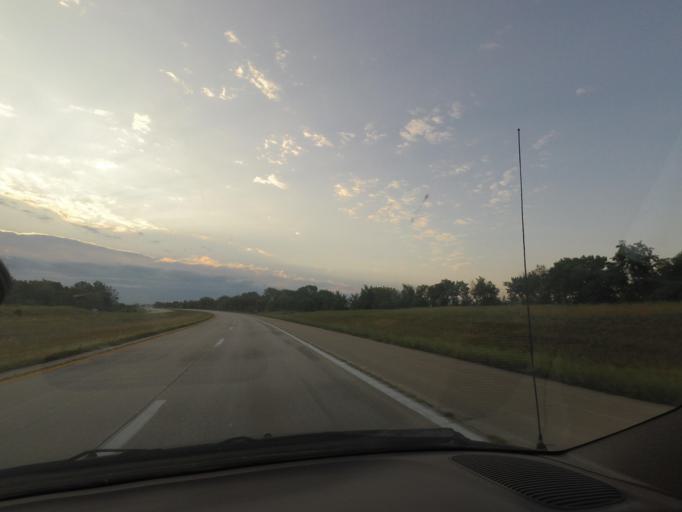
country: US
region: Missouri
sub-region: Shelby County
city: Shelbina
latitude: 39.7415
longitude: -92.2415
